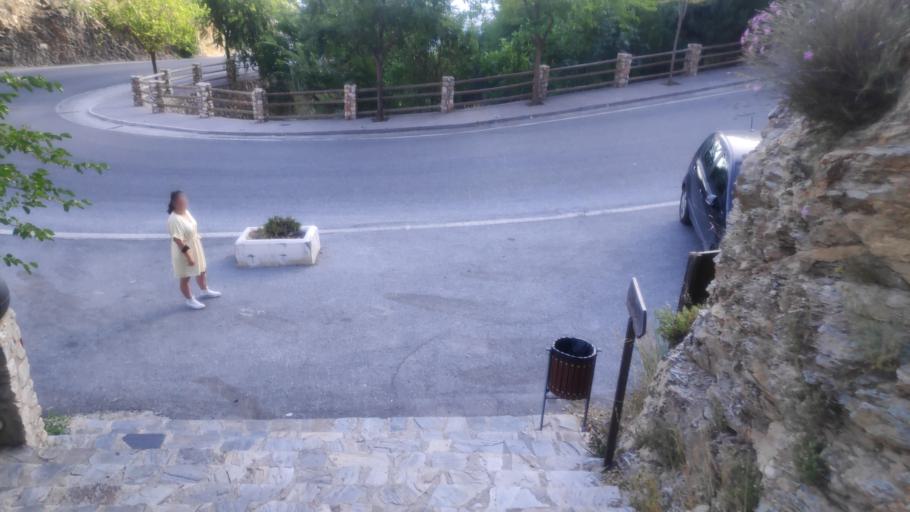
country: ES
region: Andalusia
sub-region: Provincia de Granada
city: Soportujar
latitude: 36.9265
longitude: -3.3987
